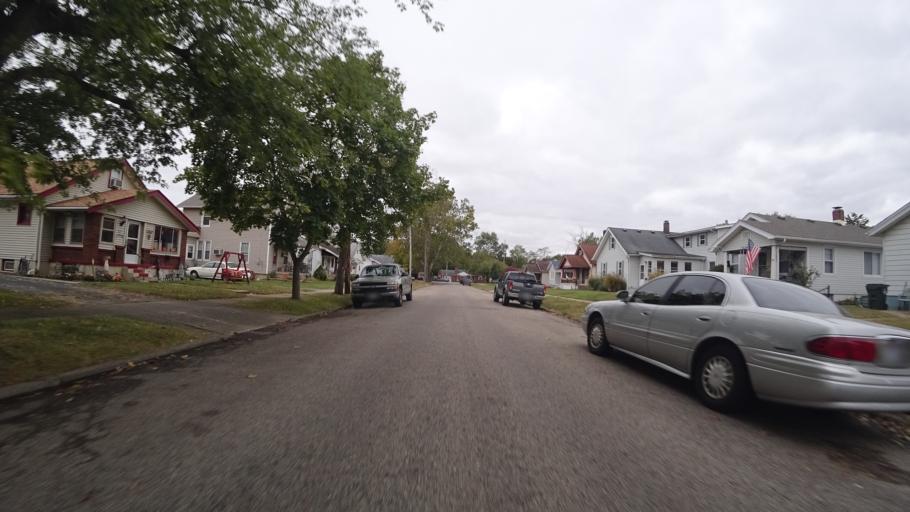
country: US
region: Ohio
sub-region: Butler County
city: Fairfield
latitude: 39.3642
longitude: -84.5614
